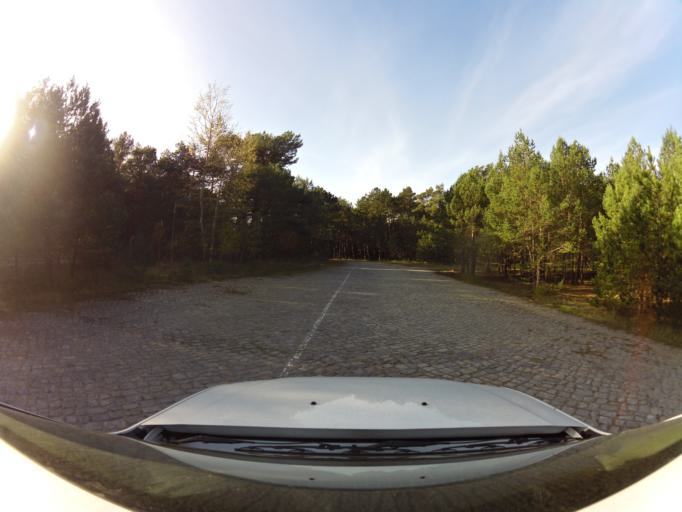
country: PL
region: West Pomeranian Voivodeship
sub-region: Powiat gryficki
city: Trzebiatow
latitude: 54.1185
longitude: 15.1798
